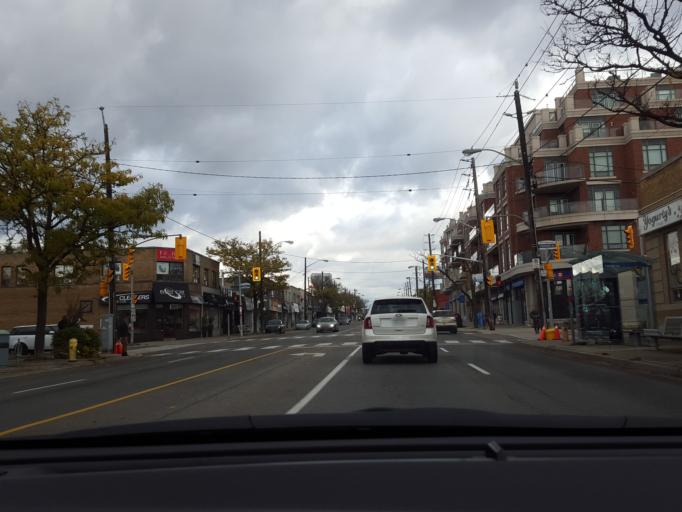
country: CA
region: Ontario
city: Toronto
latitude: 43.7275
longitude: -79.4177
